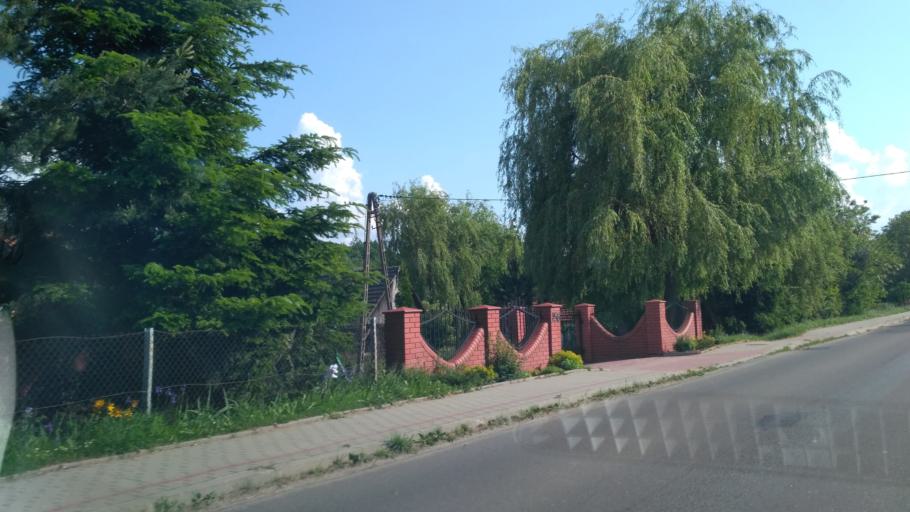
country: PL
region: Subcarpathian Voivodeship
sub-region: Powiat jaroslawski
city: Pruchnik
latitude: 49.8957
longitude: 22.5011
